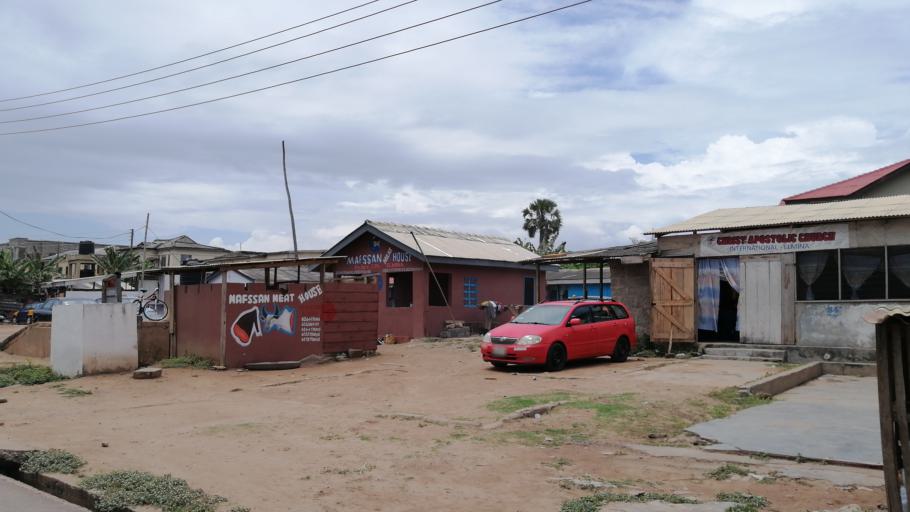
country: GH
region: Central
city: Elmina
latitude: 5.0907
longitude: -1.3454
